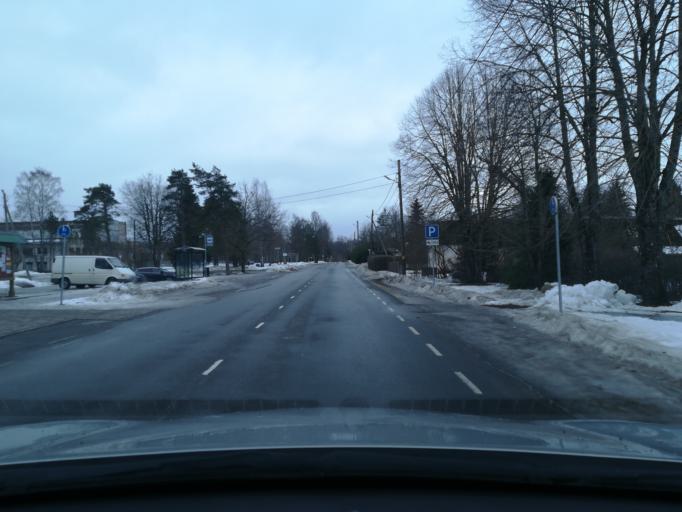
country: EE
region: Harju
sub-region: Nissi vald
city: Turba
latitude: 59.0805
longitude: 24.2361
